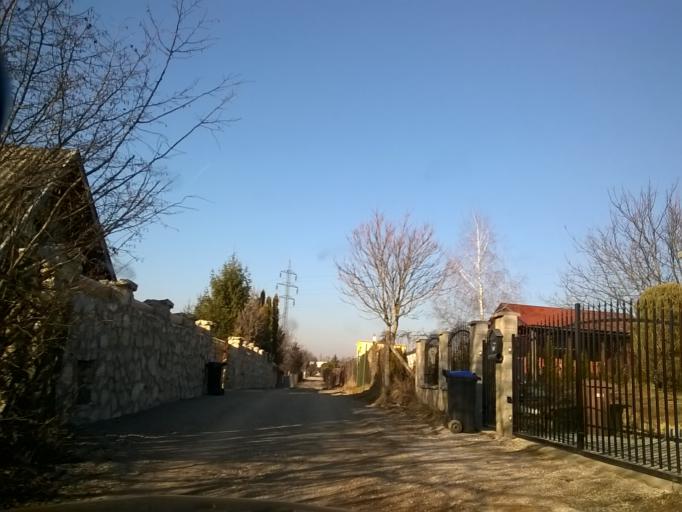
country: SK
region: Nitriansky
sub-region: Okres Nitra
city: Nitra
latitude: 48.2913
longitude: 18.0357
